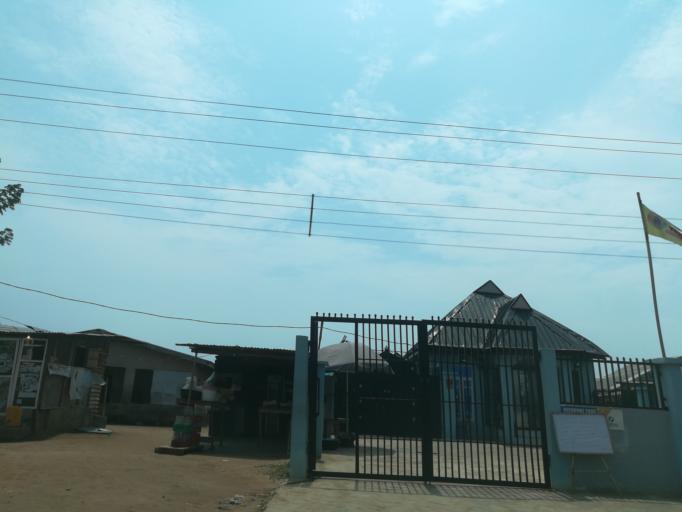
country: NG
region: Lagos
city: Ikorodu
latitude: 6.5859
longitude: 3.6251
